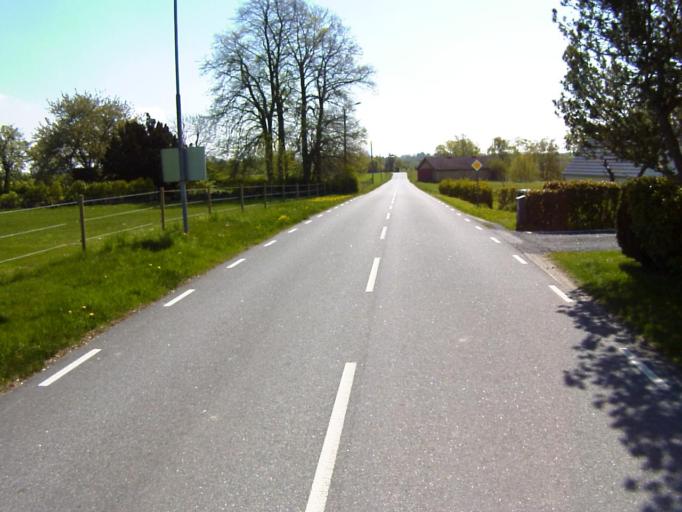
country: SE
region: Skane
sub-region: Kristianstads Kommun
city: Fjalkinge
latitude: 56.0093
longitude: 14.2463
